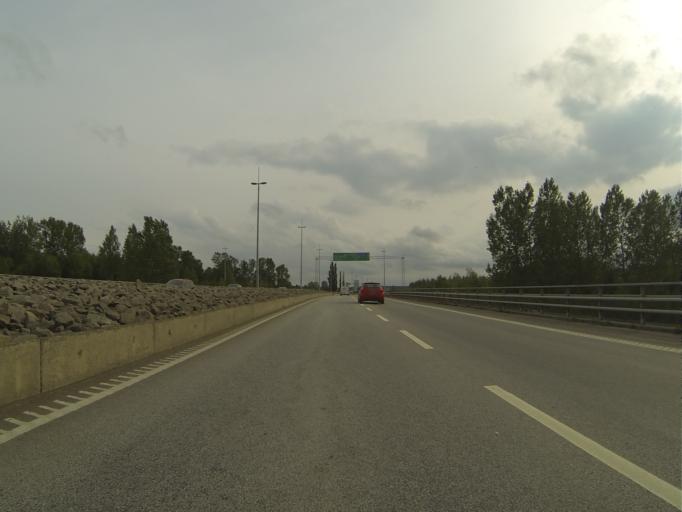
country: SE
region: Skane
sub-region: Kristianstads Kommun
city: Kristianstad
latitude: 56.0187
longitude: 14.1165
